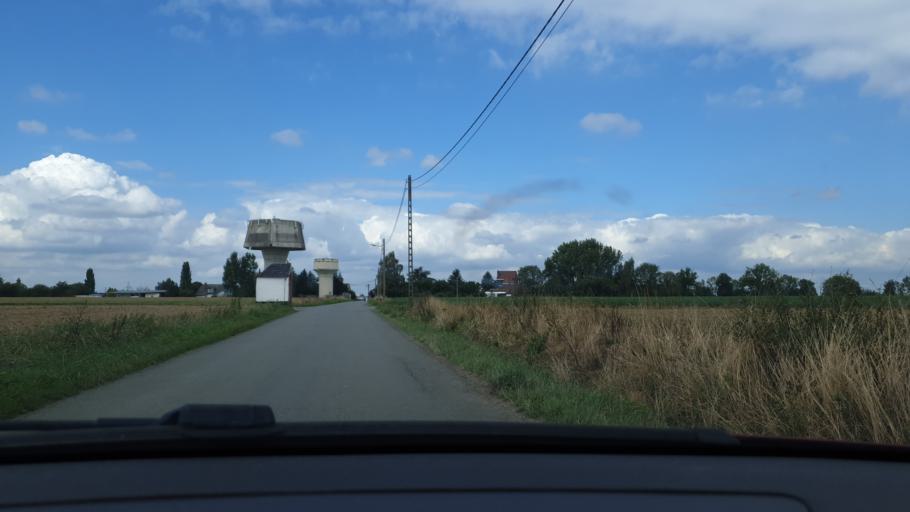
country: BE
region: Wallonia
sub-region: Province du Hainaut
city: Enghien
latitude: 50.6872
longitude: 4.0709
